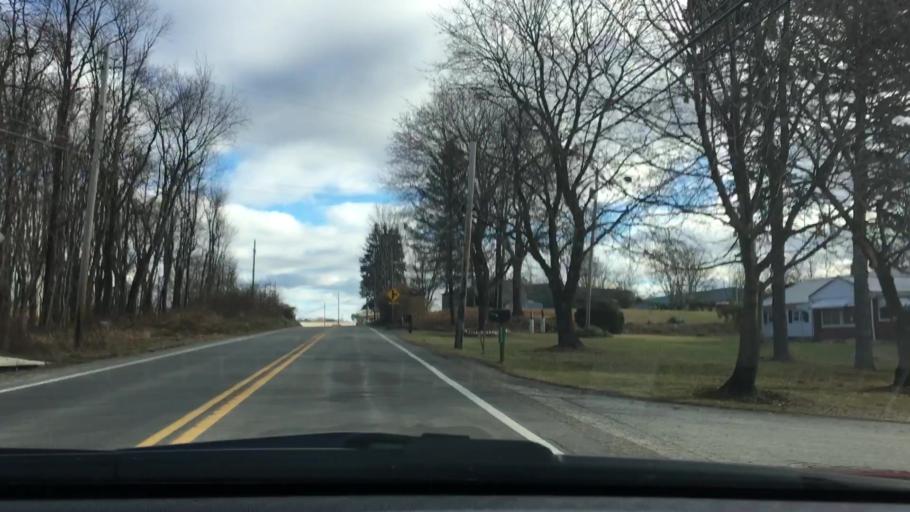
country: US
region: Pennsylvania
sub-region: Westmoreland County
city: Avonmore
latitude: 40.6068
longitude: -79.4464
